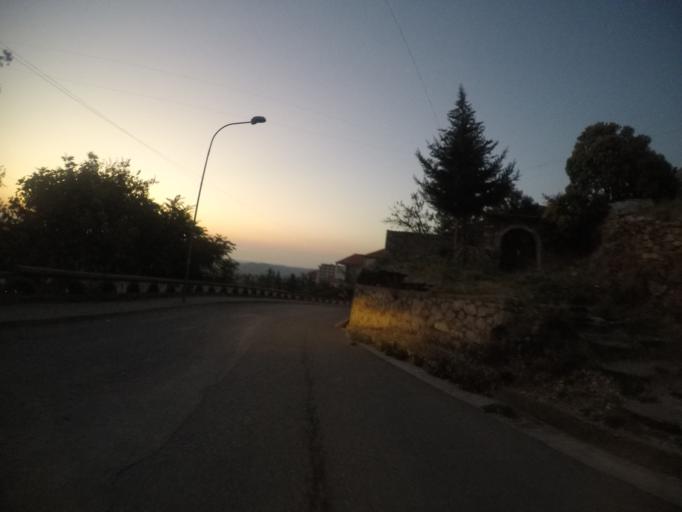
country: AL
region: Durres
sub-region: Rrethi i Krujes
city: Kruje
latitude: 41.5122
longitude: 19.7927
